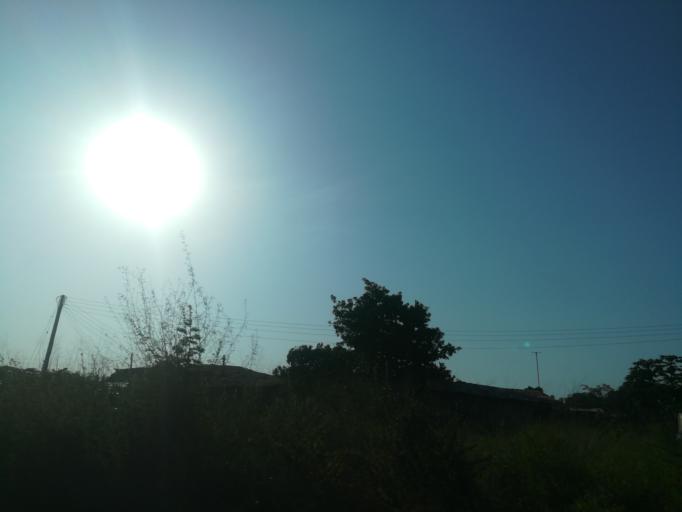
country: NG
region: Ogun
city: Abeokuta
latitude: 7.2386
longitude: 3.3008
